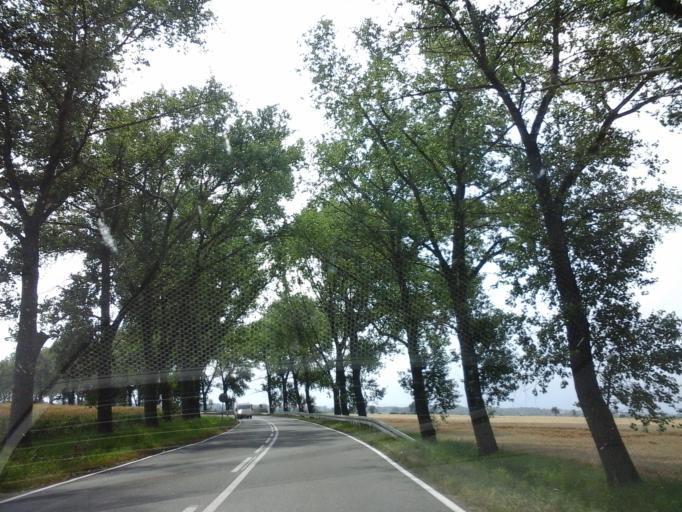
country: PL
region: Lower Silesian Voivodeship
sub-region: Powiat strzelinski
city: Strzelin
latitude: 50.8560
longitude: 17.0610
